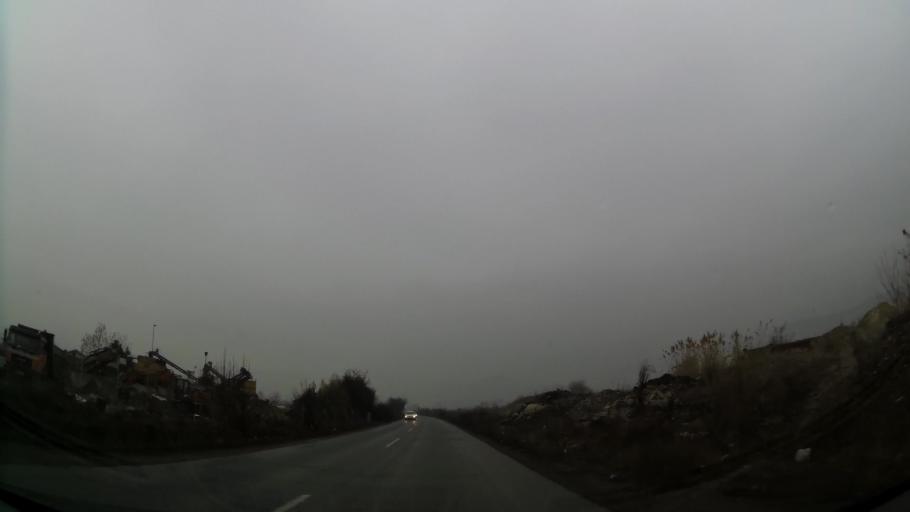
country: MK
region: Cucer-Sandevo
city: Chucher - Sandevo
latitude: 42.0614
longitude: 21.3738
